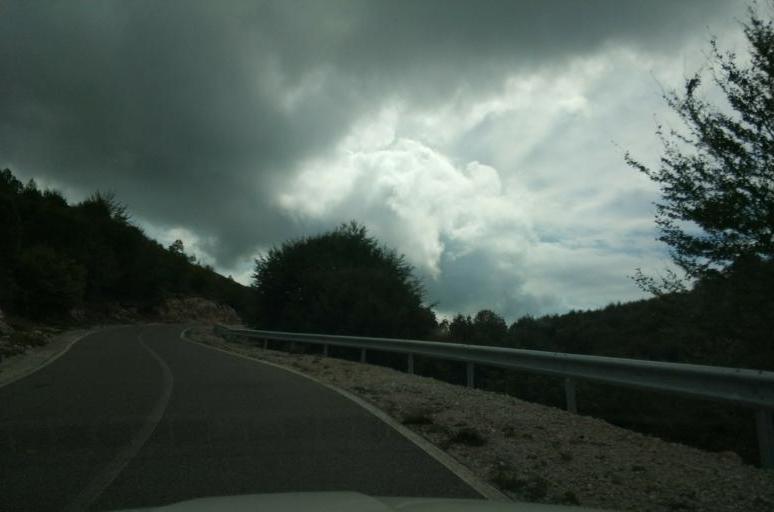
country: AL
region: Durres
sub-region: Rrethi i Krujes
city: Kruje
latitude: 41.5196
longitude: 19.8065
